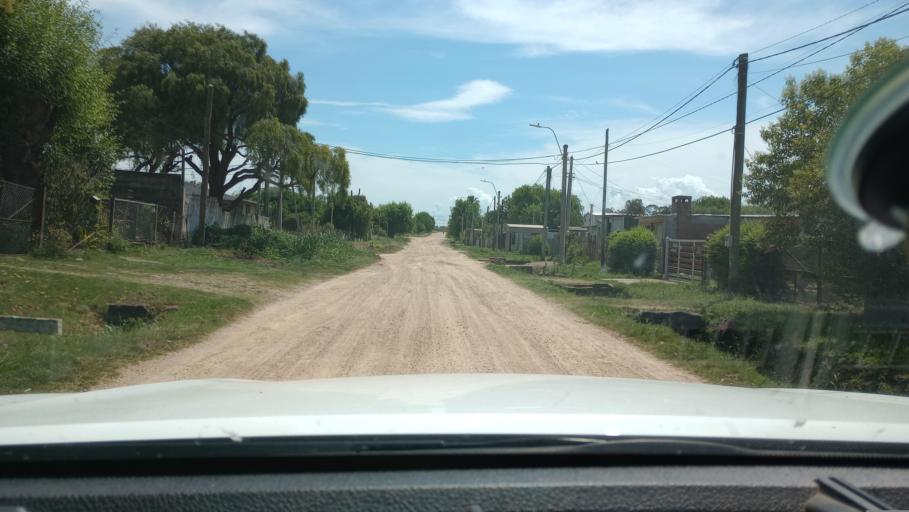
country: UY
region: Canelones
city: Joaquin Suarez
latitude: -34.7517
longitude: -56.0150
